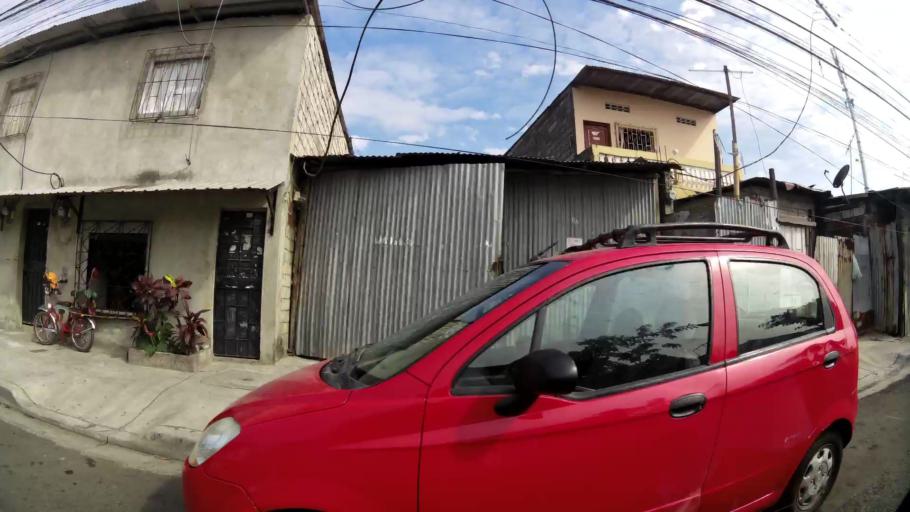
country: EC
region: Guayas
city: Guayaquil
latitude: -2.2600
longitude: -79.8748
